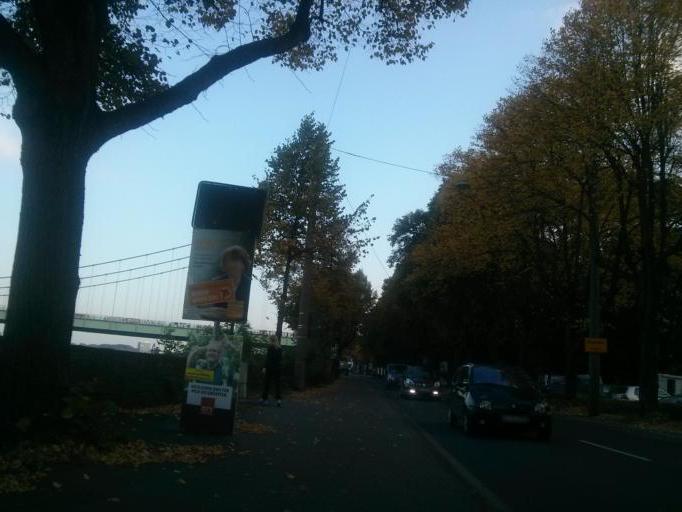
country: DE
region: North Rhine-Westphalia
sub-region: Regierungsbezirk Koln
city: Poll
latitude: 50.8999
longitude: 6.9856
